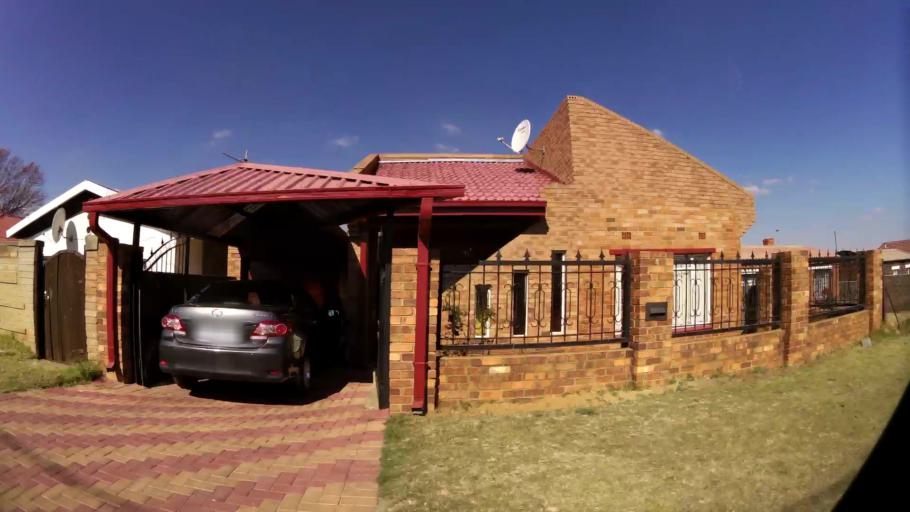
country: ZA
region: Gauteng
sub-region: City of Johannesburg Metropolitan Municipality
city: Soweto
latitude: -26.2391
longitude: 27.8978
